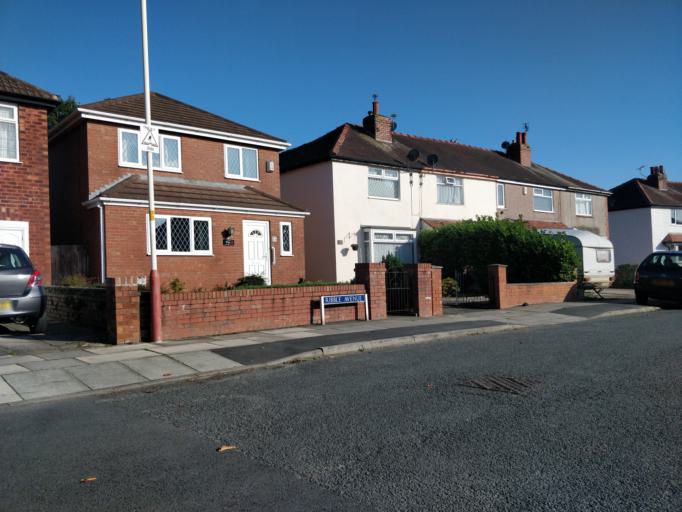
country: GB
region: England
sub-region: Lancashire
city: Banks
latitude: 53.6720
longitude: -2.9529
